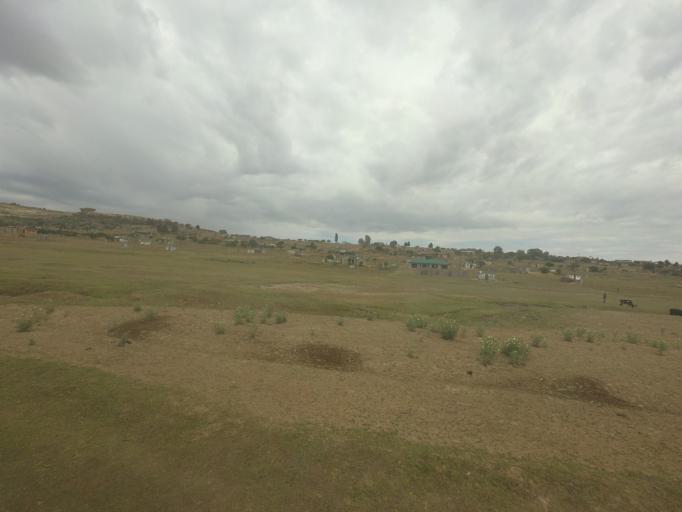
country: LS
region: Leribe
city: Leribe
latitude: -29.0250
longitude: 28.0213
